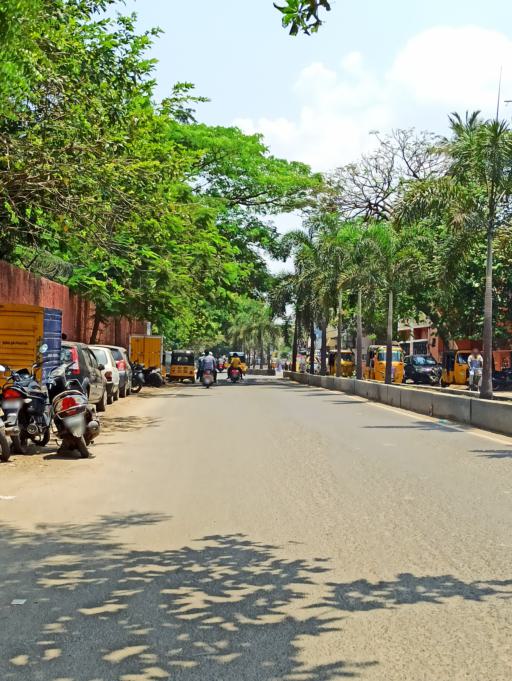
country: IN
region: Tamil Nadu
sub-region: Chennai
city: Chetput
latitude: 13.0920
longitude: 80.2319
